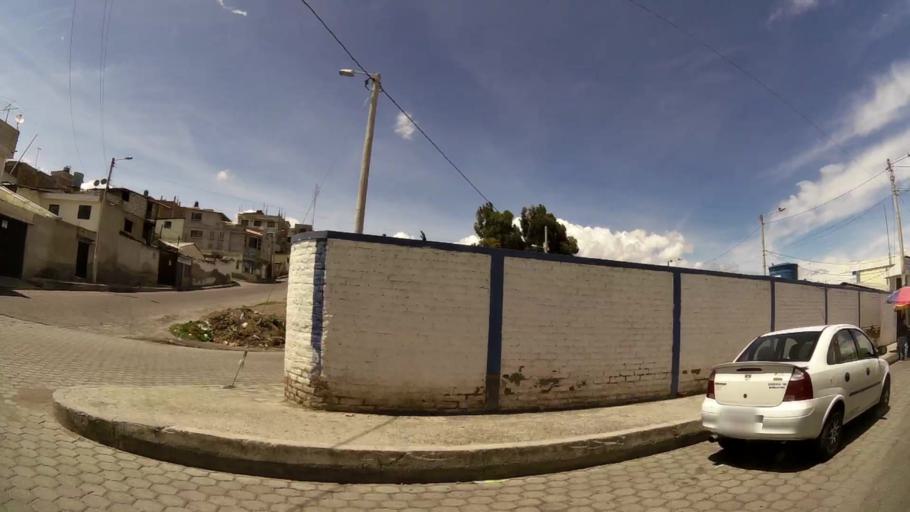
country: EC
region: Chimborazo
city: Riobamba
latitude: -1.6612
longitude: -78.6414
